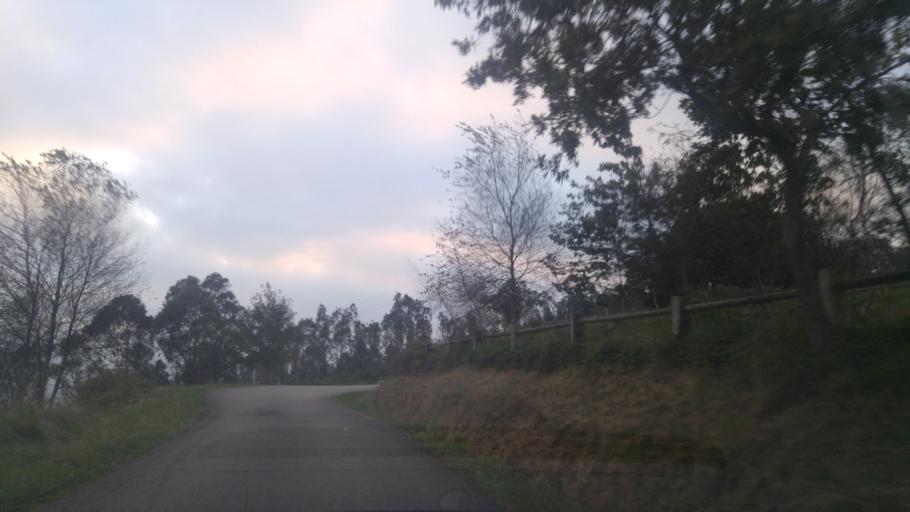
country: ES
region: Asturias
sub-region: Province of Asturias
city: Oviedo
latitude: 43.3846
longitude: -5.8610
